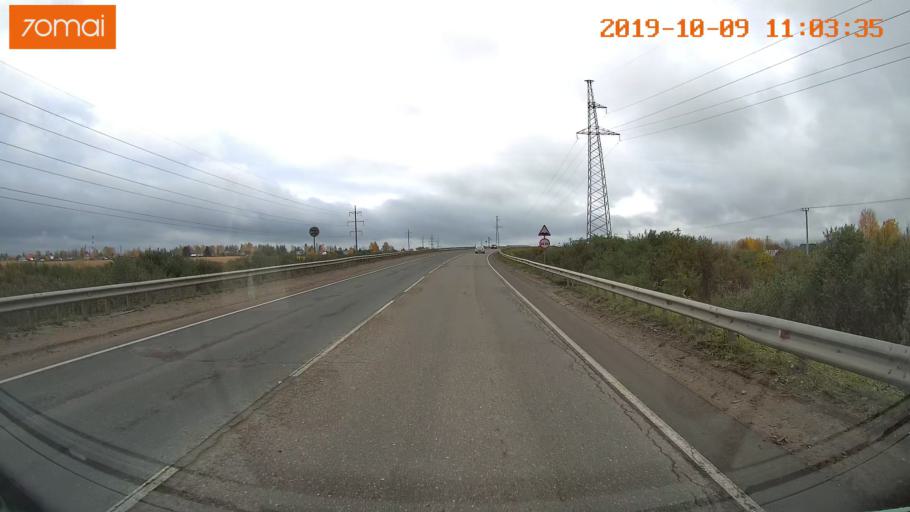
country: RU
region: Vologda
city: Vologda
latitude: 59.2195
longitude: 39.7738
